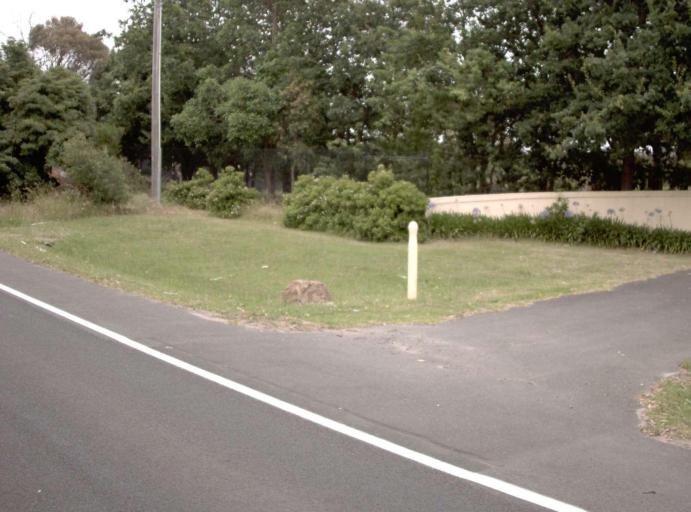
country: AU
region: Victoria
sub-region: Mornington Peninsula
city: Mount Martha
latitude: -38.2757
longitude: 145.0329
